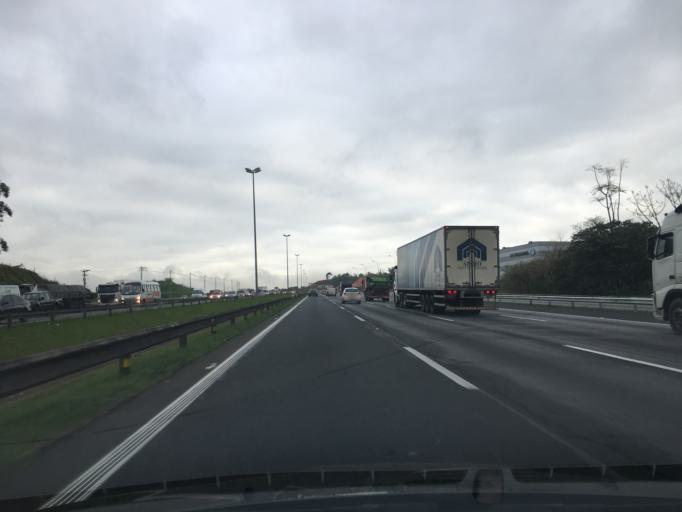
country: BR
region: Sao Paulo
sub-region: Osasco
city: Osasco
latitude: -23.5575
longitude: -46.8196
